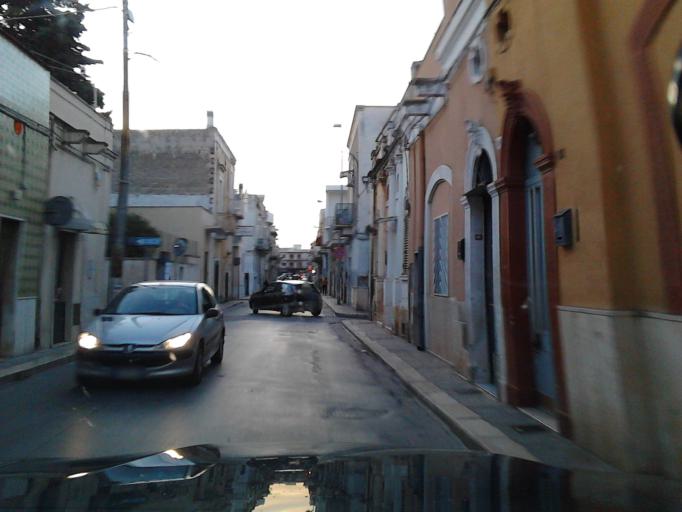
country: IT
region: Apulia
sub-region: Provincia di Bari
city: Valenzano
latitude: 41.0442
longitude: 16.8876
